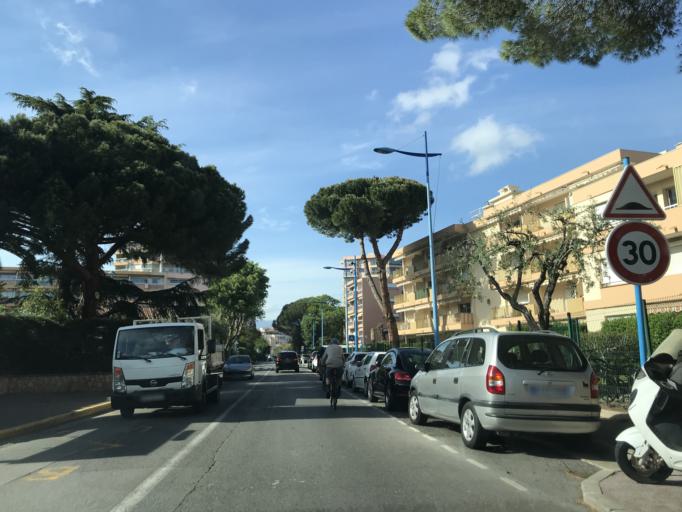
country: FR
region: Provence-Alpes-Cote d'Azur
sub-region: Departement des Alpes-Maritimes
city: Mandelieu-la-Napoule
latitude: 43.5422
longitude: 6.9424
